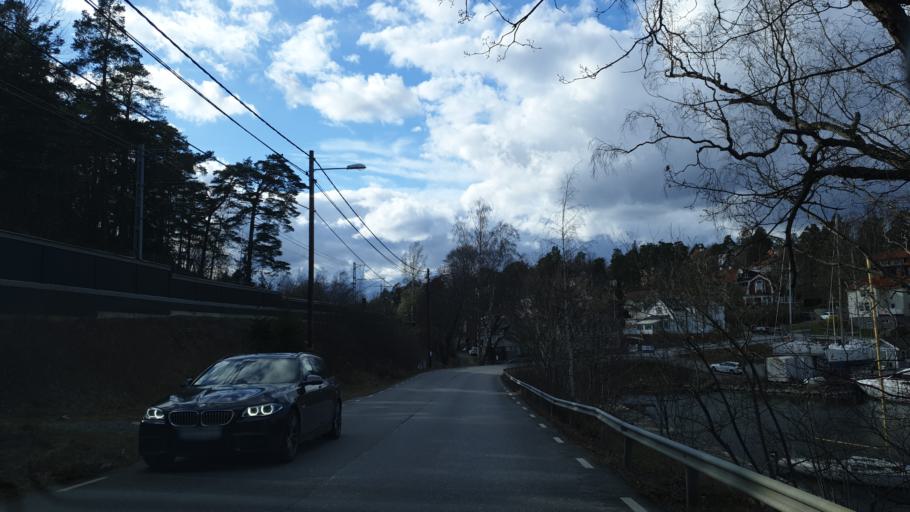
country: SE
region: Stockholm
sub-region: Nacka Kommun
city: Alta
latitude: 59.2998
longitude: 18.2037
